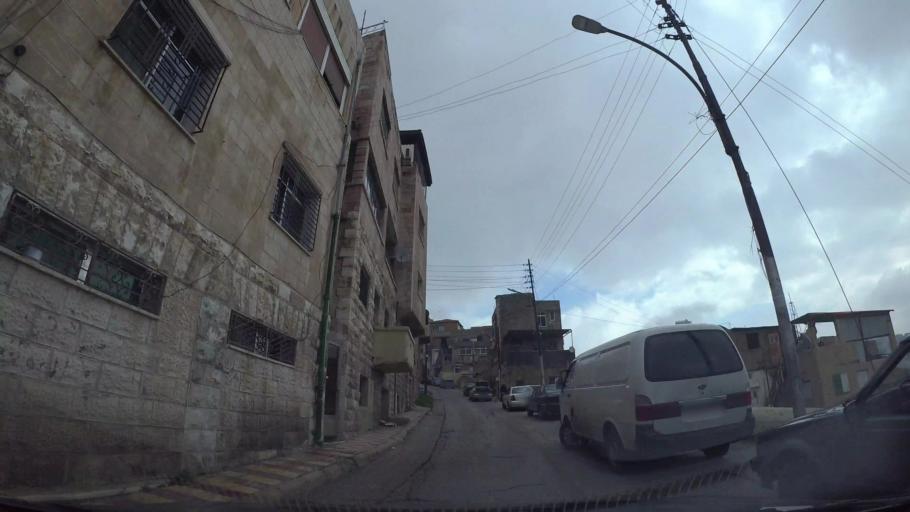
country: JO
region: Amman
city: Amman
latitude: 31.9473
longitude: 35.9221
